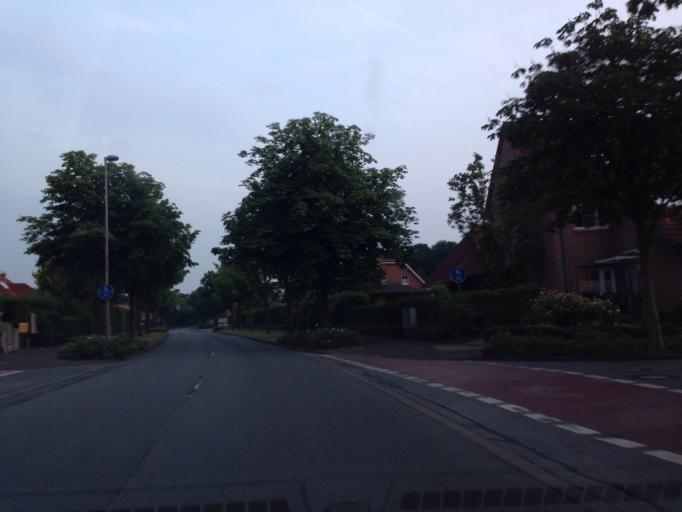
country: DE
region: North Rhine-Westphalia
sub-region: Regierungsbezirk Munster
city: Senden
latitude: 51.8638
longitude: 7.4807
